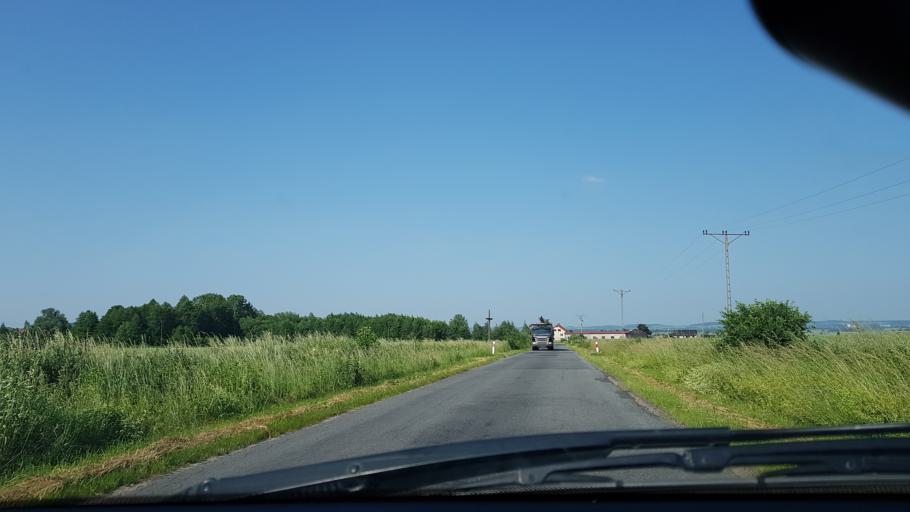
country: PL
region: Lower Silesian Voivodeship
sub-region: Powiat zabkowicki
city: Budzow
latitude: 50.5696
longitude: 16.6756
